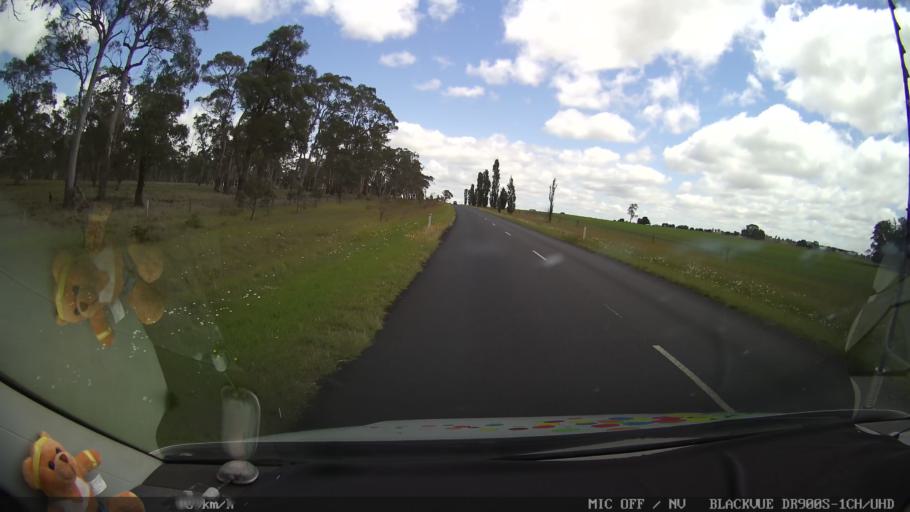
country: AU
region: New South Wales
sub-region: Glen Innes Severn
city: Glen Innes
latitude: -29.6652
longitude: 151.6937
